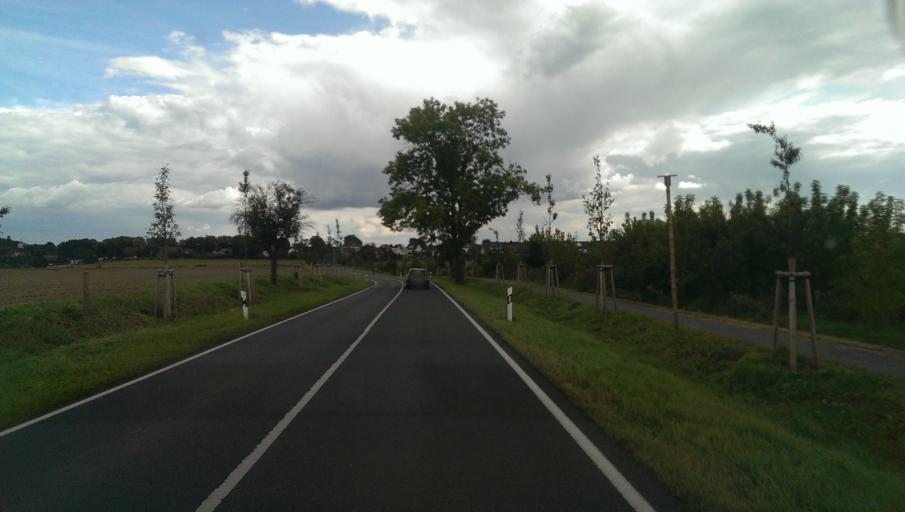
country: DE
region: Brandenburg
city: Velten
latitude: 52.6801
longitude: 13.1297
